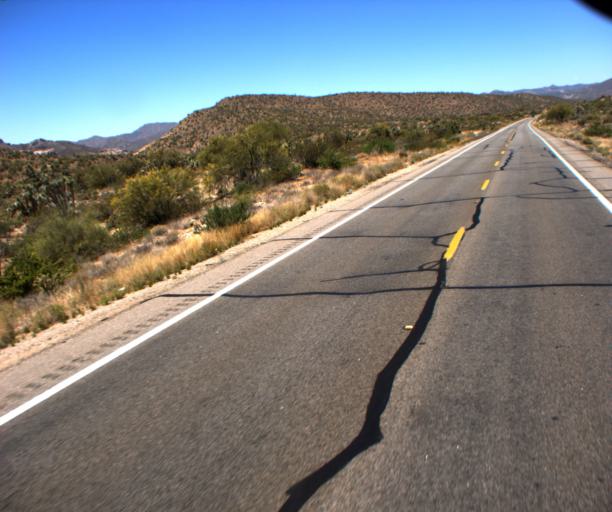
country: US
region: Arizona
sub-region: Yavapai County
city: Bagdad
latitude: 34.3431
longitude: -113.1564
